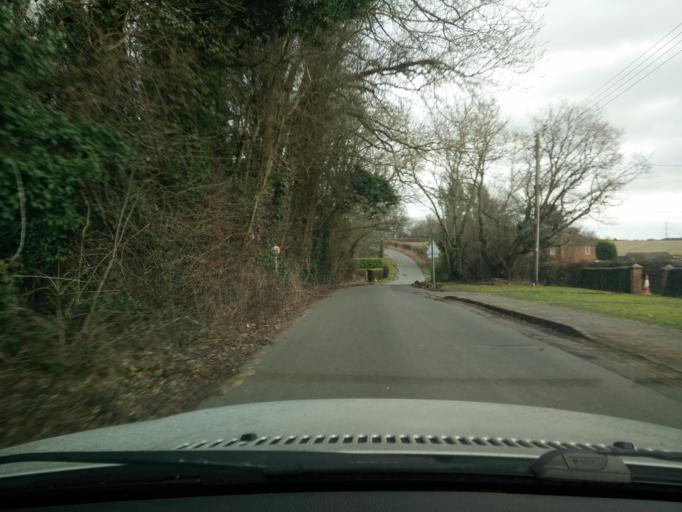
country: GB
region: England
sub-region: Buckinghamshire
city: Amersham
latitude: 51.6585
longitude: -0.6632
